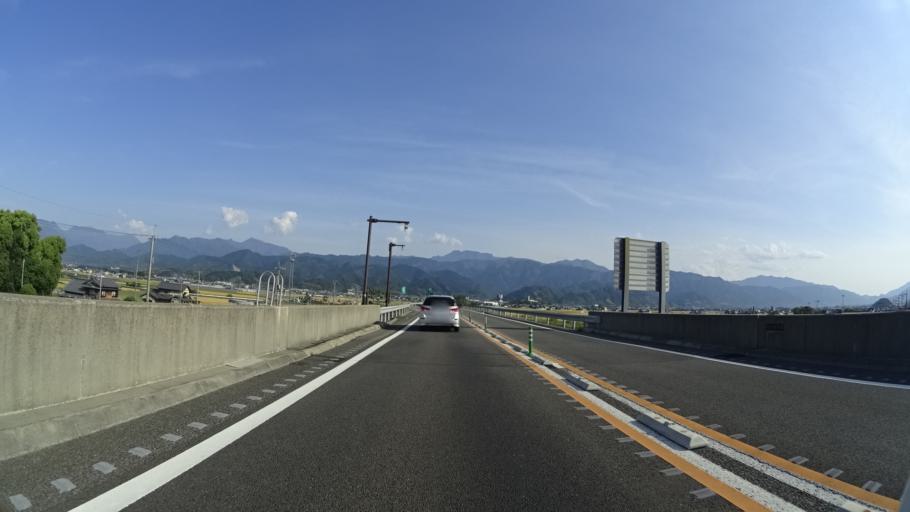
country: JP
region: Ehime
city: Saijo
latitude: 33.9103
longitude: 133.0731
